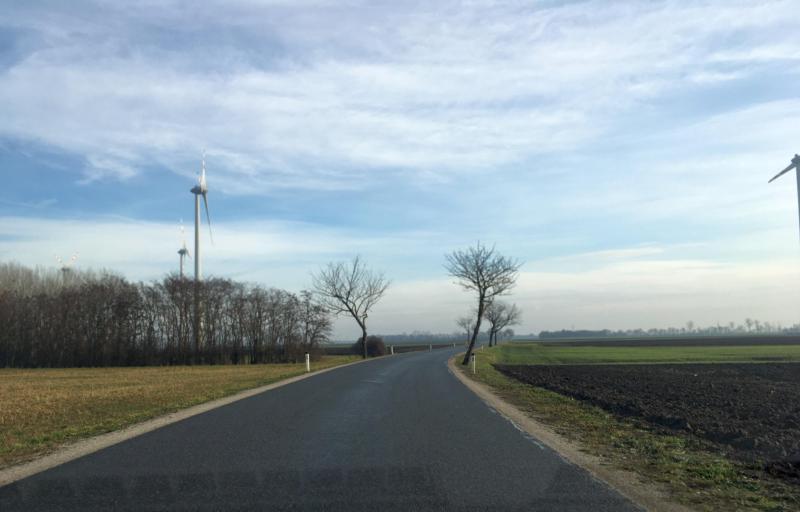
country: AT
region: Lower Austria
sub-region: Politischer Bezirk Ganserndorf
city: Andlersdorf
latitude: 48.1944
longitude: 16.6725
